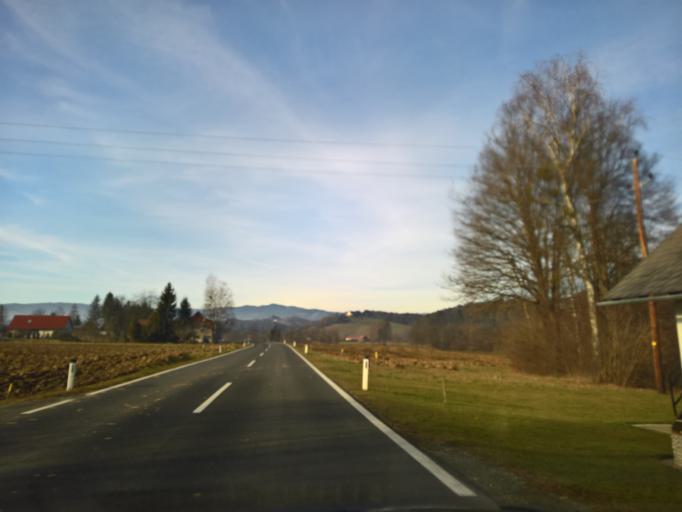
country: AT
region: Styria
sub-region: Politischer Bezirk Leibnitz
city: Oberhaag
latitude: 46.6988
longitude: 15.3021
